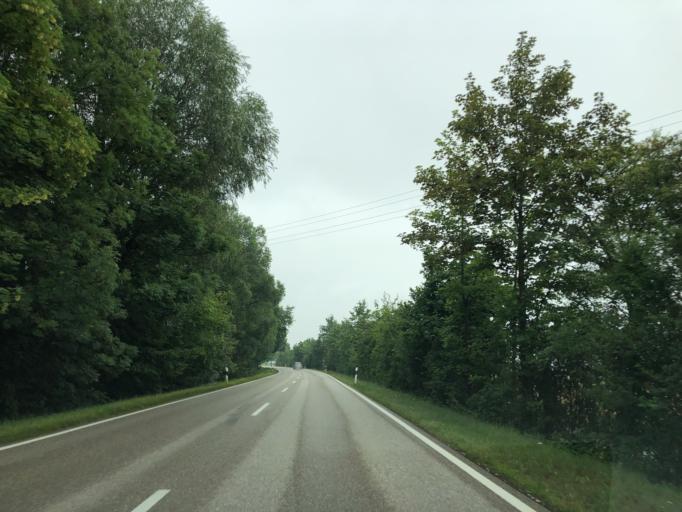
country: DE
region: Bavaria
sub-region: Upper Bavaria
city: Worth
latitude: 48.2570
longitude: 11.9268
